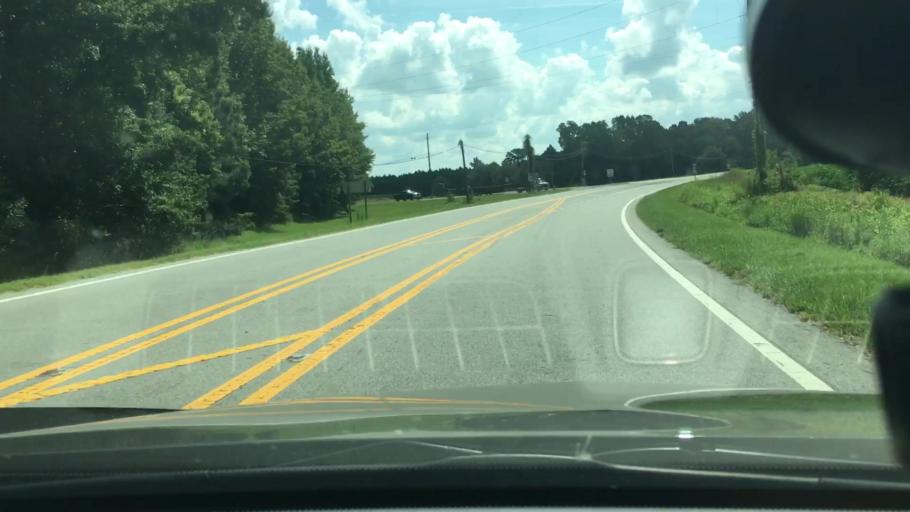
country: US
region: North Carolina
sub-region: Pitt County
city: Farmville
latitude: 35.6944
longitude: -77.5006
